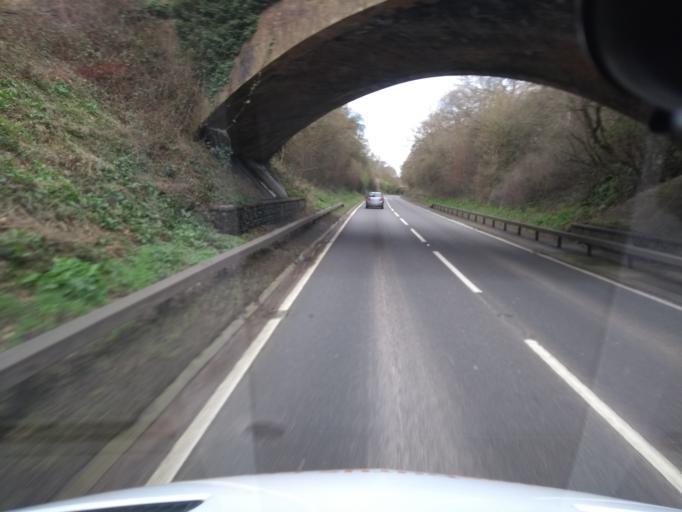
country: GB
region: England
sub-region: Somerset
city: Yeovil
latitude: 50.9427
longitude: -2.6830
